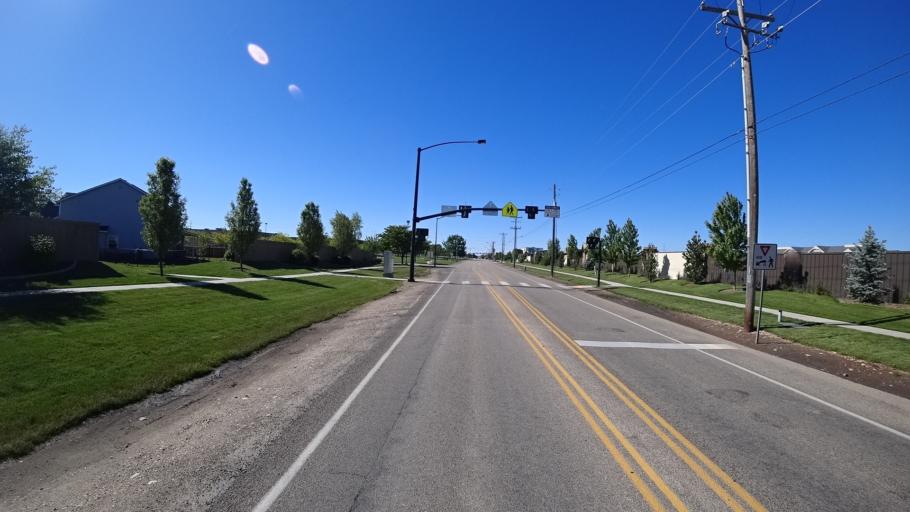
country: US
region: Idaho
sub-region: Ada County
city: Meridian
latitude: 43.6517
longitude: -116.3936
